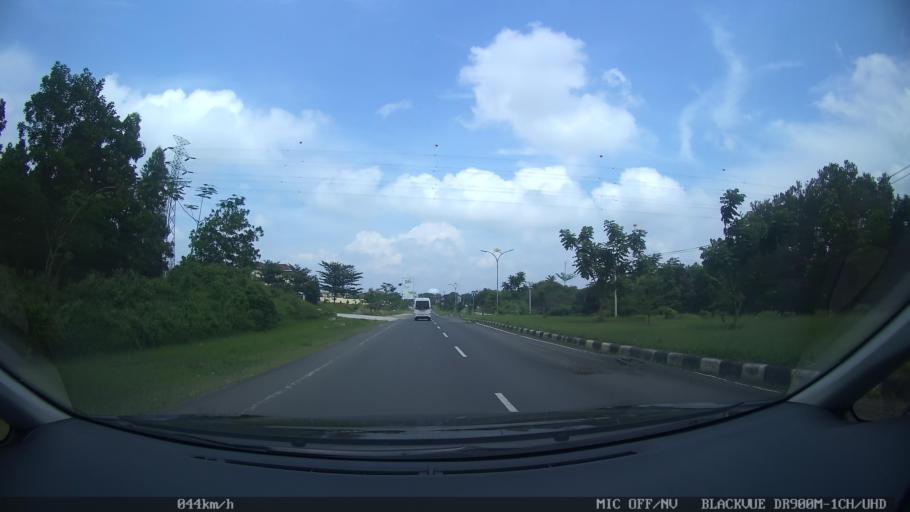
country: ID
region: Lampung
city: Kedaton
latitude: -5.3580
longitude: 105.3099
